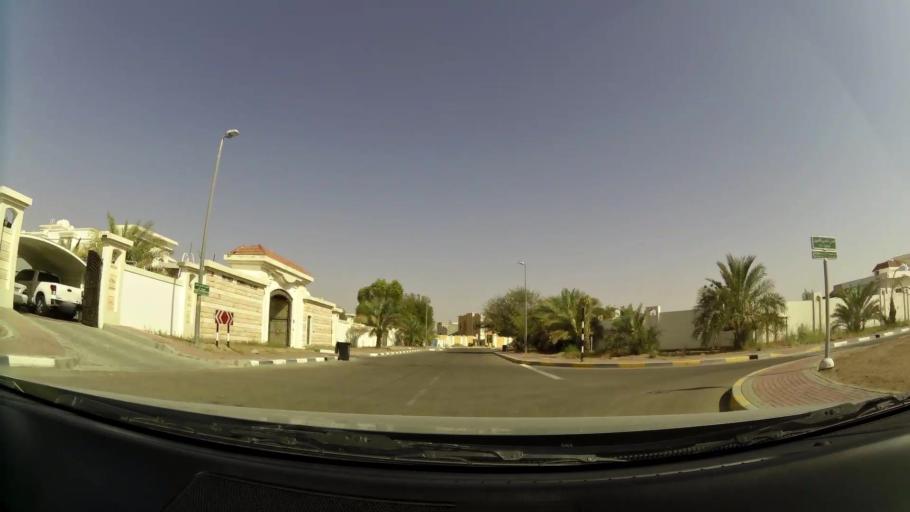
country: OM
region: Al Buraimi
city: Al Buraymi
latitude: 24.3339
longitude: 55.7939
